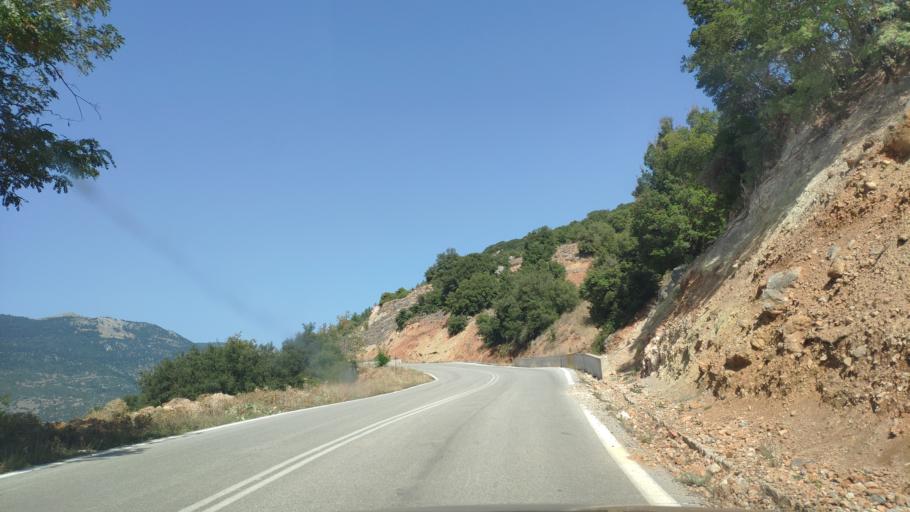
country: GR
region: West Greece
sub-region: Nomos Achaias
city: Aiyira
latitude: 37.9217
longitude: 22.3388
